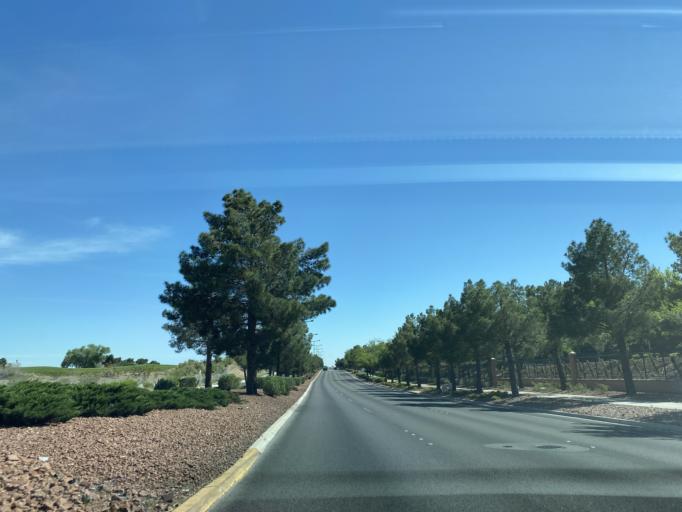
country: US
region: Nevada
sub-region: Clark County
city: Summerlin South
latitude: 36.1858
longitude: -115.2876
